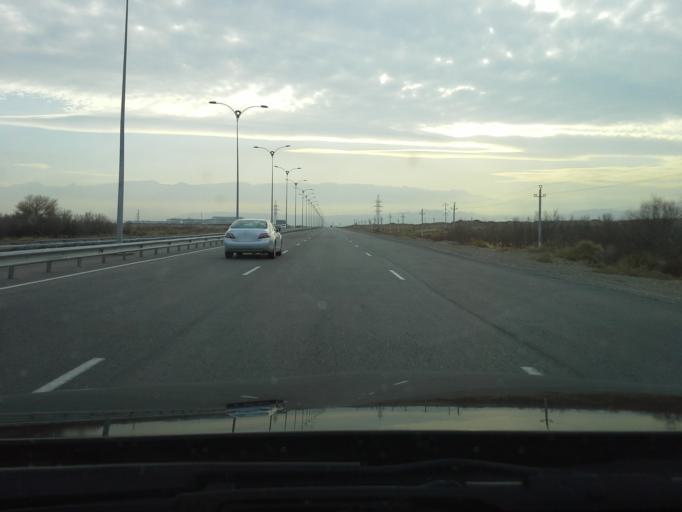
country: TM
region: Ahal
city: Abadan
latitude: 38.0735
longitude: 58.3177
